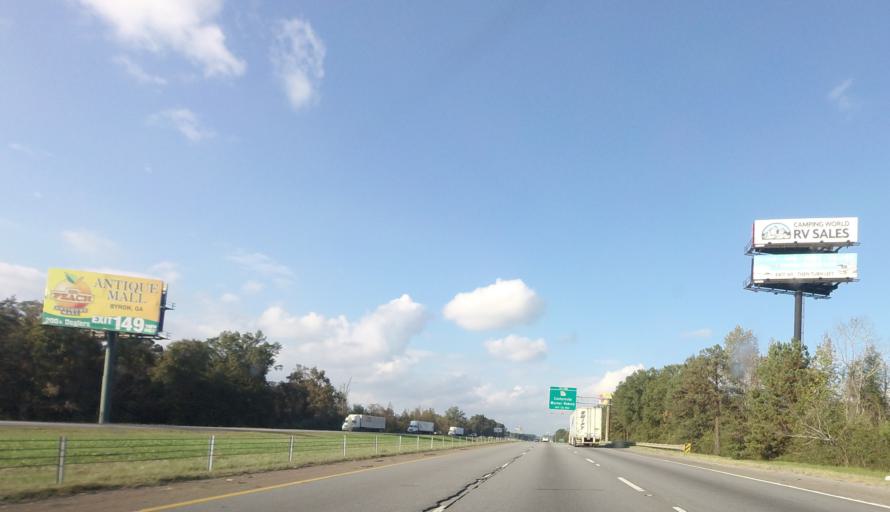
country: US
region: Georgia
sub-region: Peach County
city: Byron
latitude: 32.6026
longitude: -83.7424
